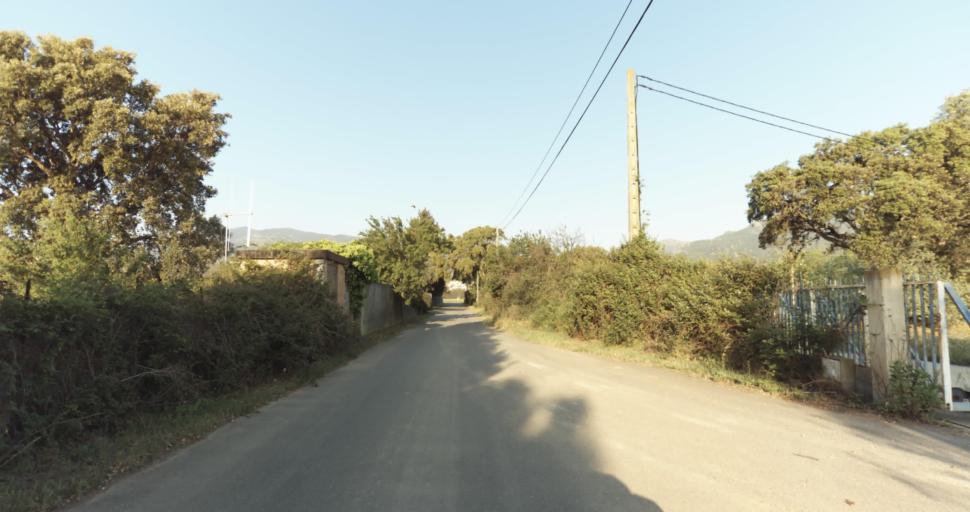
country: FR
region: Corsica
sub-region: Departement de la Haute-Corse
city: Biguglia
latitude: 42.6097
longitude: 9.4457
